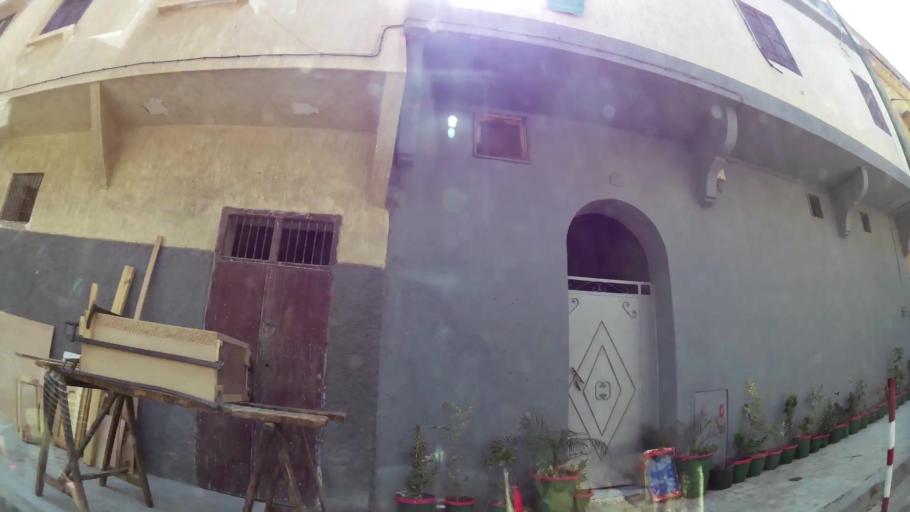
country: MA
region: Rabat-Sale-Zemmour-Zaer
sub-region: Rabat
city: Rabat
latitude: 34.0092
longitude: -6.8630
